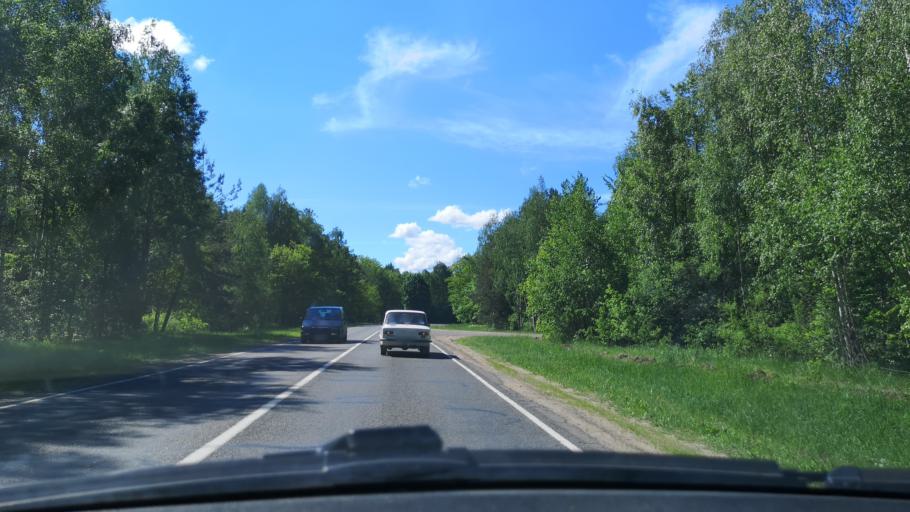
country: BY
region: Brest
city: Brest
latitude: 52.0237
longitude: 23.7301
